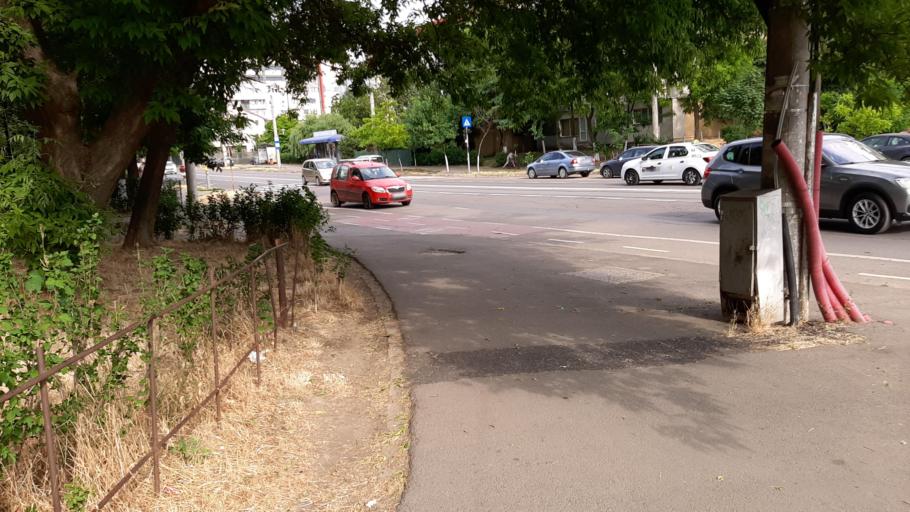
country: RO
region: Galati
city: Galati
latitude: 45.4408
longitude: 28.0290
